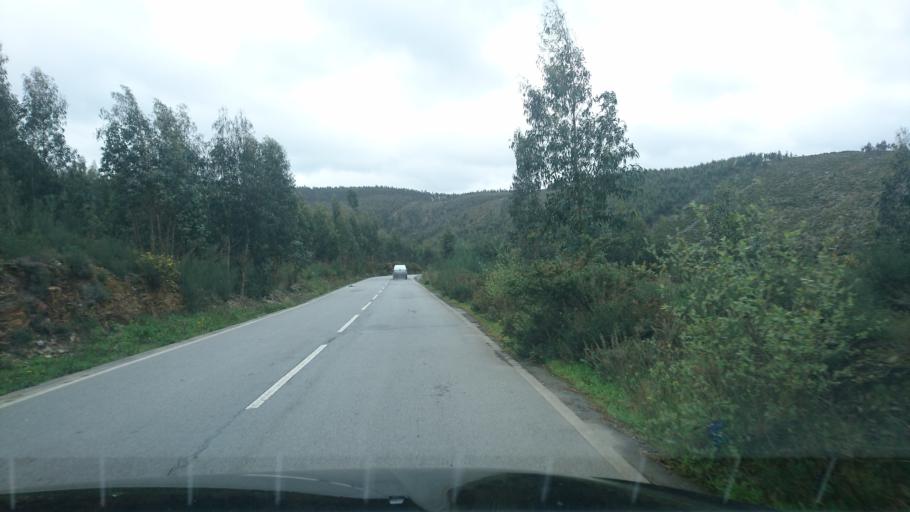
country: PT
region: Porto
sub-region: Paredes
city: Recarei
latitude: 41.1328
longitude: -8.4004
